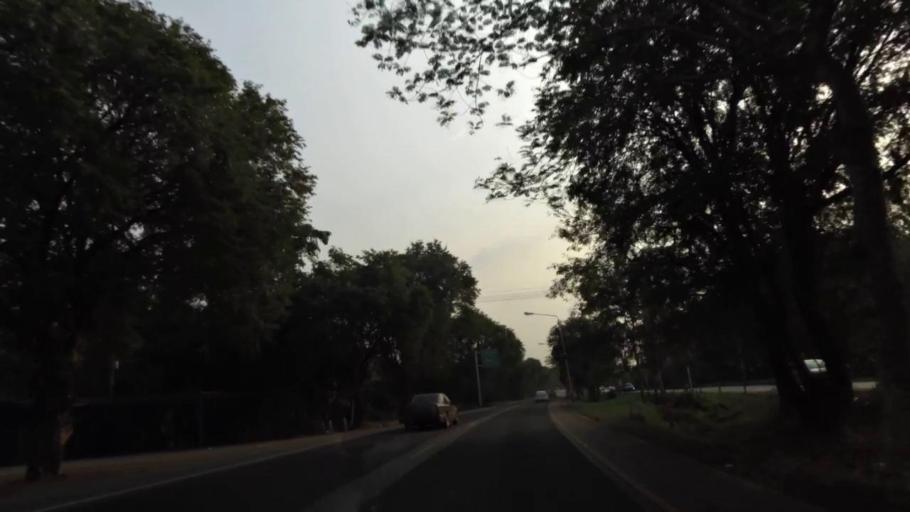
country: TH
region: Chanthaburi
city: Chanthaburi
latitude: 12.5702
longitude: 102.1625
